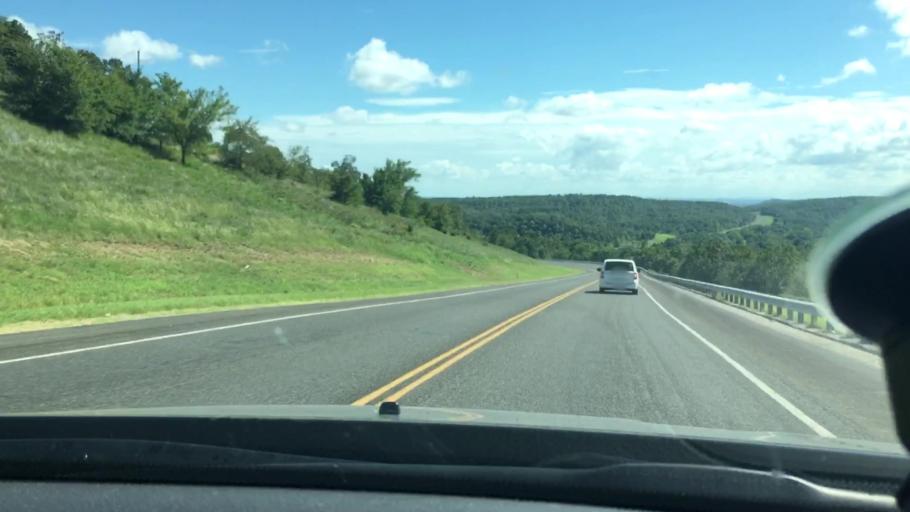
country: US
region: Oklahoma
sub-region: Sequoyah County
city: Vian
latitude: 35.5485
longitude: -94.9698
